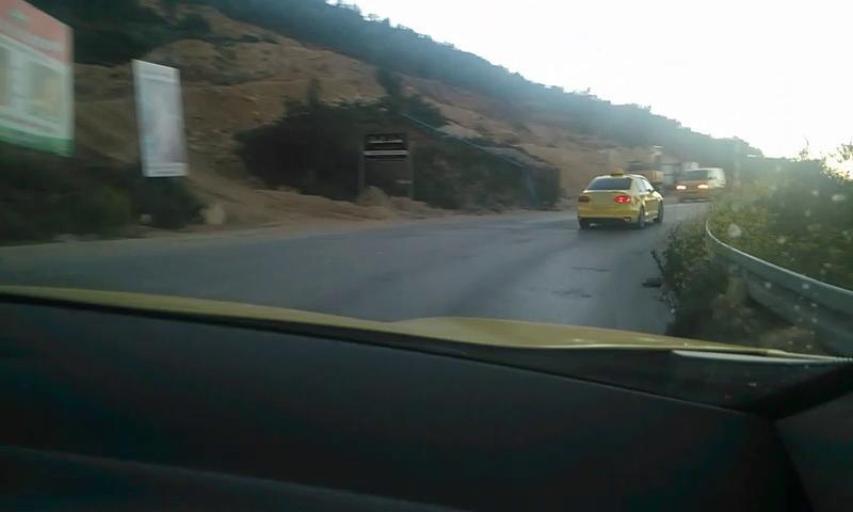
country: PS
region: West Bank
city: Dura al Qar`
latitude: 31.9570
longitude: 35.2233
